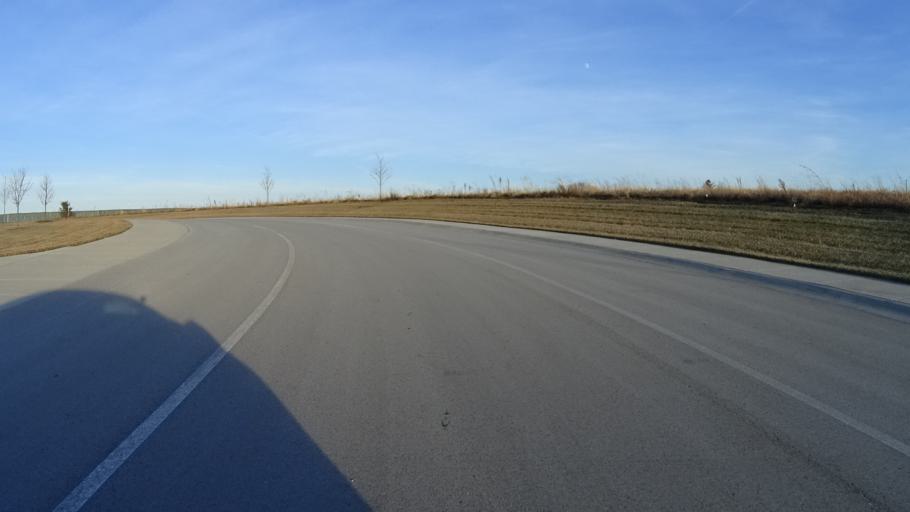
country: US
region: Nebraska
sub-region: Sarpy County
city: Springfield
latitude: 41.1336
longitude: -96.1326
